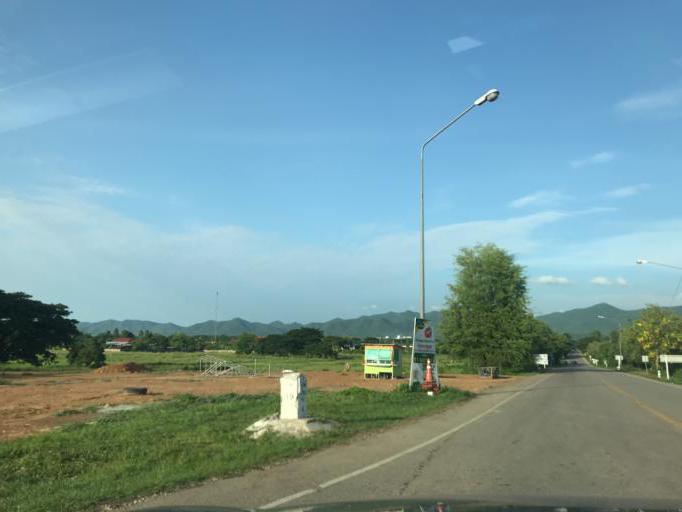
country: TH
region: Phayao
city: Phu Kam Yao
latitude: 19.3122
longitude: 100.0037
